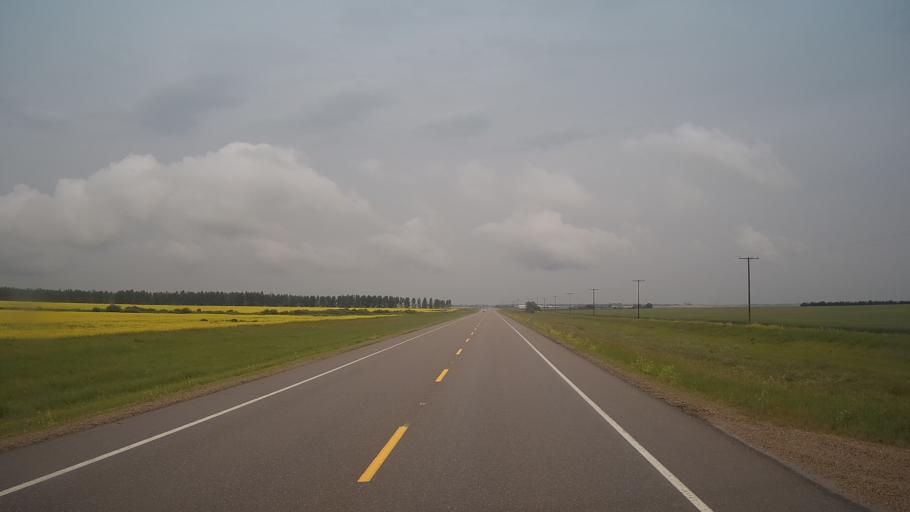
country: CA
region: Saskatchewan
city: Wilkie
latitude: 52.3402
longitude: -108.7138
